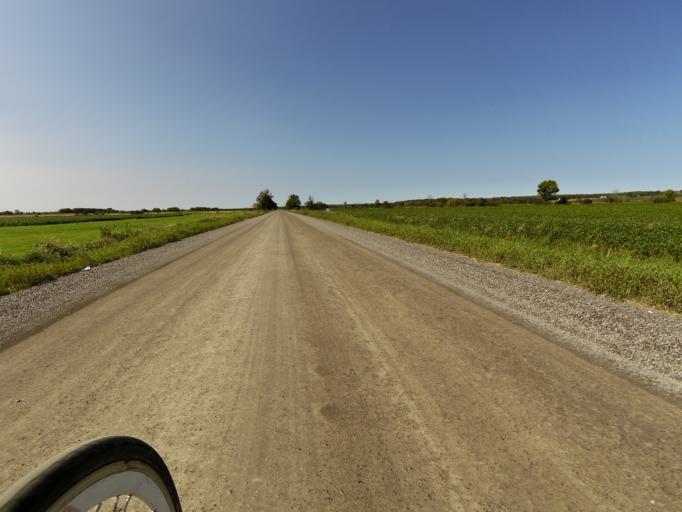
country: CA
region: Ontario
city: Arnprior
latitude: 45.3698
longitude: -76.1373
